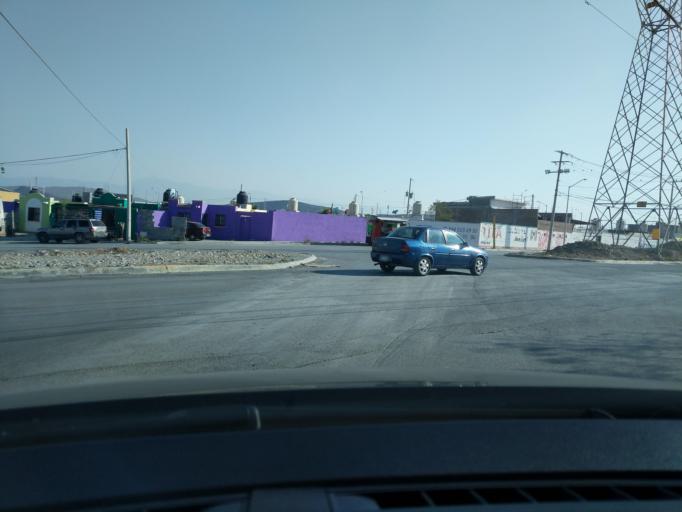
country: MX
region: Coahuila
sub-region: Ramos Arizpe
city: Ramos Arizpe
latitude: 25.5455
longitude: -100.9670
